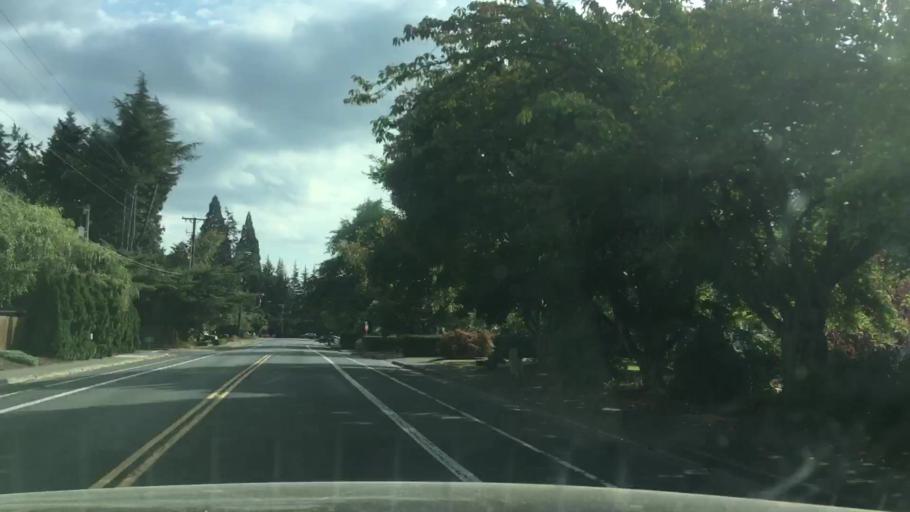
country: US
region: Oregon
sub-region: Lane County
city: Eugene
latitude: 44.0857
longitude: -123.0881
